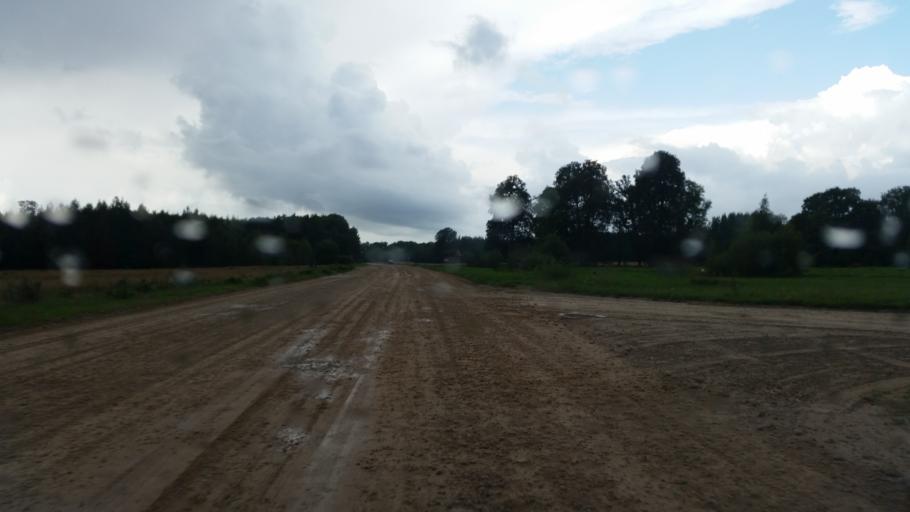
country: LV
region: Vecumnieki
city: Vecumnieki
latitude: 56.4310
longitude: 24.4512
